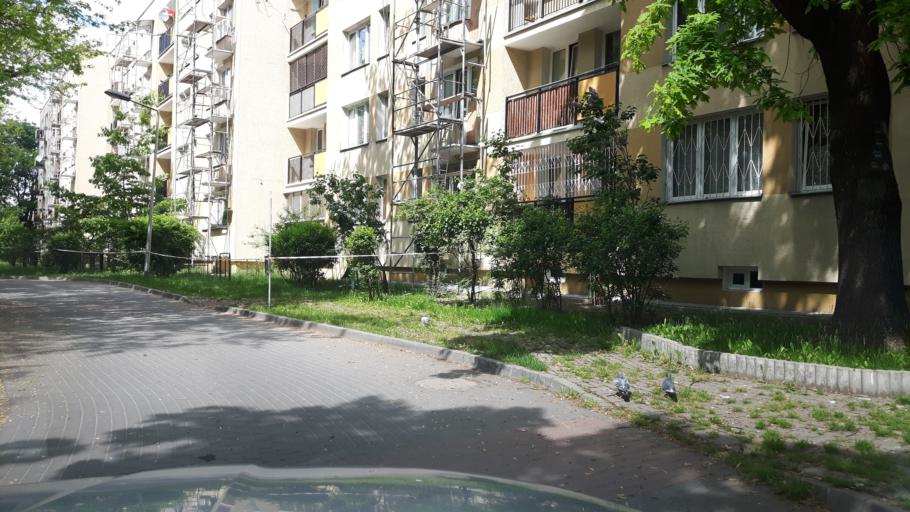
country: PL
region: Masovian Voivodeship
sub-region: Warszawa
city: Targowek
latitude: 52.2954
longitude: 21.0249
